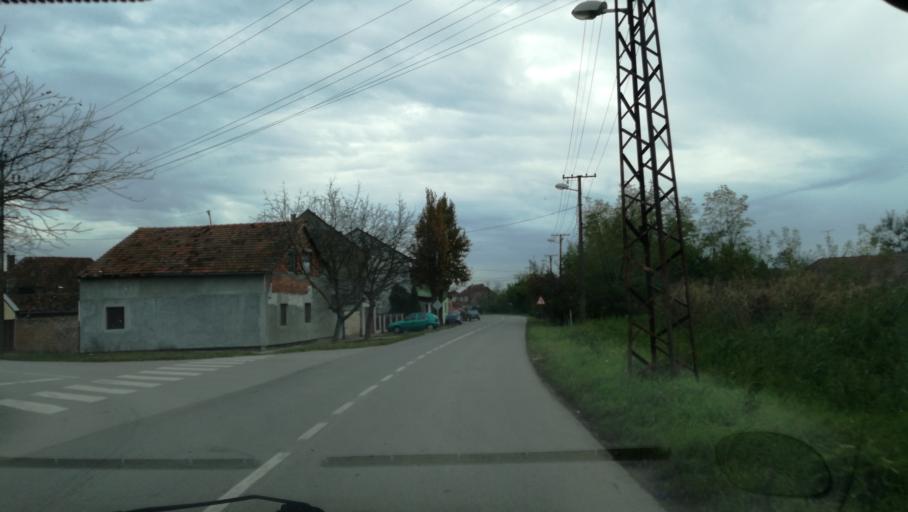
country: RS
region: Autonomna Pokrajina Vojvodina
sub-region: Severnobanatski Okrug
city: Kikinda
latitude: 45.8431
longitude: 20.4689
